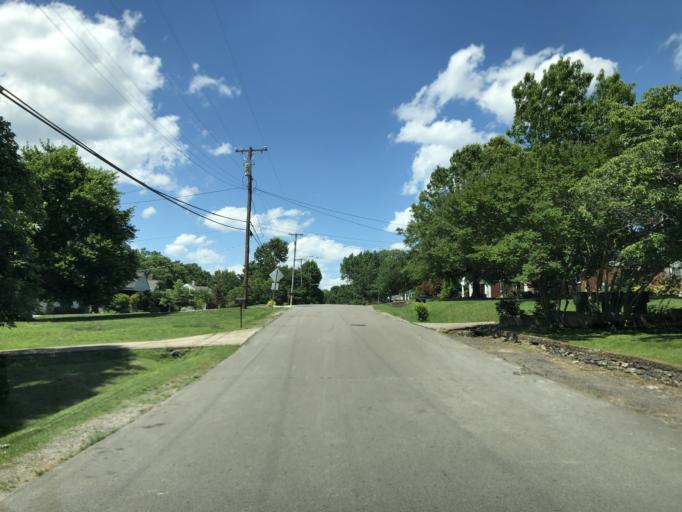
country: US
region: Tennessee
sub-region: Davidson County
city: Nashville
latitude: 36.1789
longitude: -86.7318
